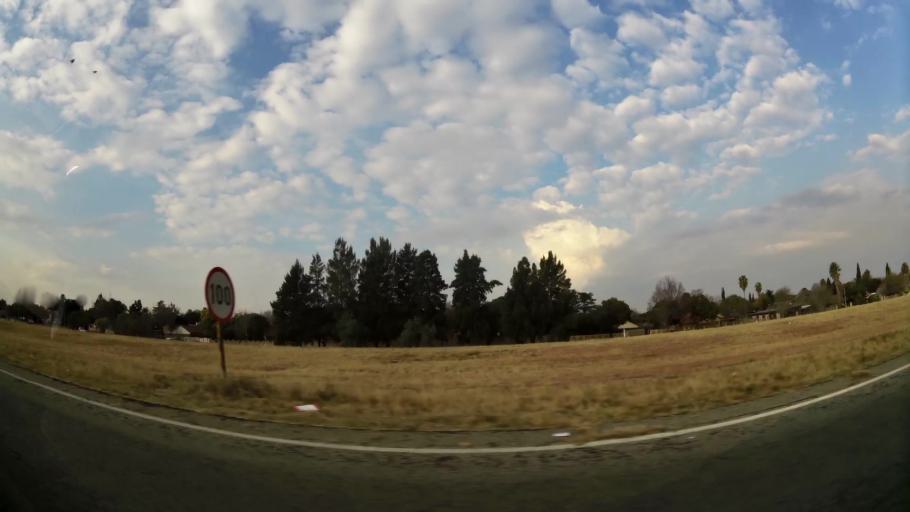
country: ZA
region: Gauteng
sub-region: Sedibeng District Municipality
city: Vanderbijlpark
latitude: -26.7299
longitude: 27.8210
